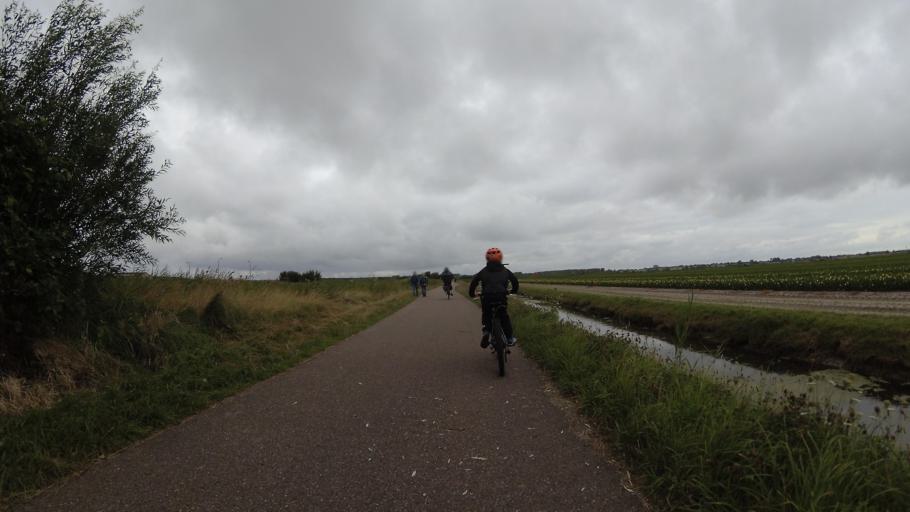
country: NL
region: North Holland
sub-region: Gemeente Den Helder
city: Den Helder
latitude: 52.9192
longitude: 4.7289
